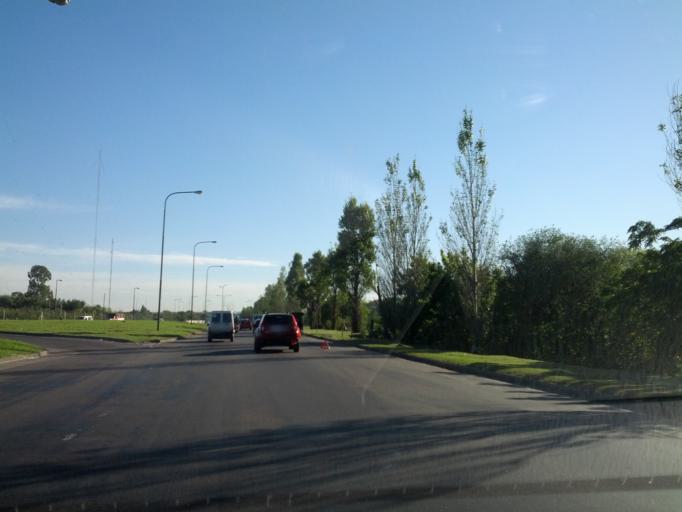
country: AR
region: Buenos Aires F.D.
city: Villa Lugano
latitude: -34.6735
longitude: -58.4349
